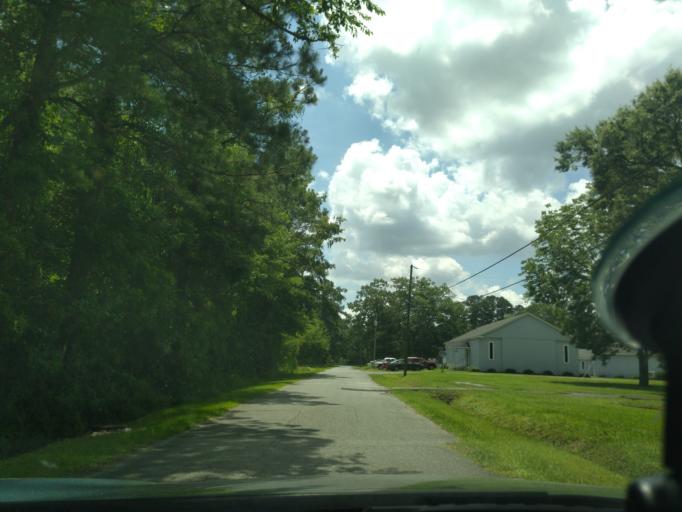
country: US
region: North Carolina
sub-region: Washington County
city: Plymouth
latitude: 35.8510
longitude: -76.7614
